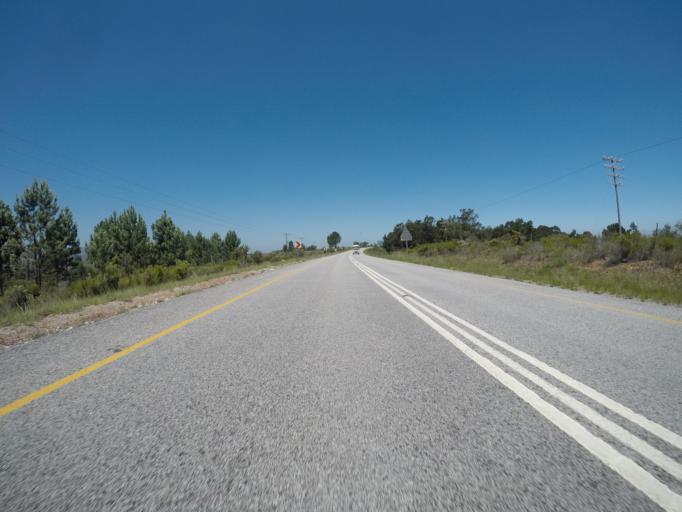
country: ZA
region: Eastern Cape
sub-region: Cacadu District Municipality
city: Kruisfontein
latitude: -33.9881
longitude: 24.5250
